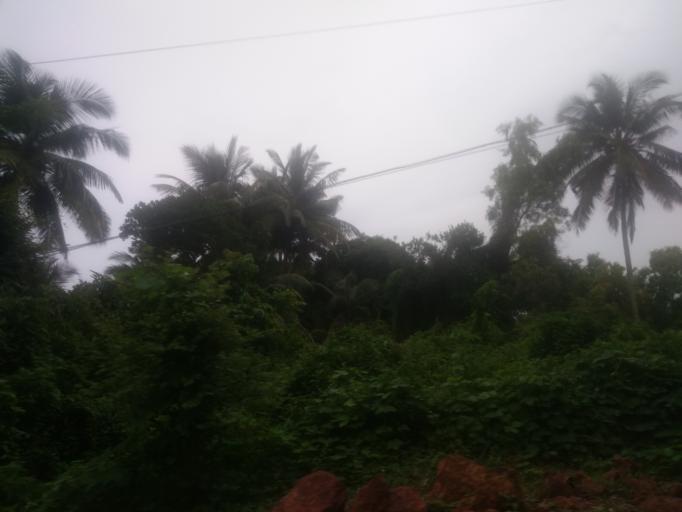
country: IN
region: Goa
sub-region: South Goa
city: Varca
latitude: 15.2062
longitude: 73.9472
